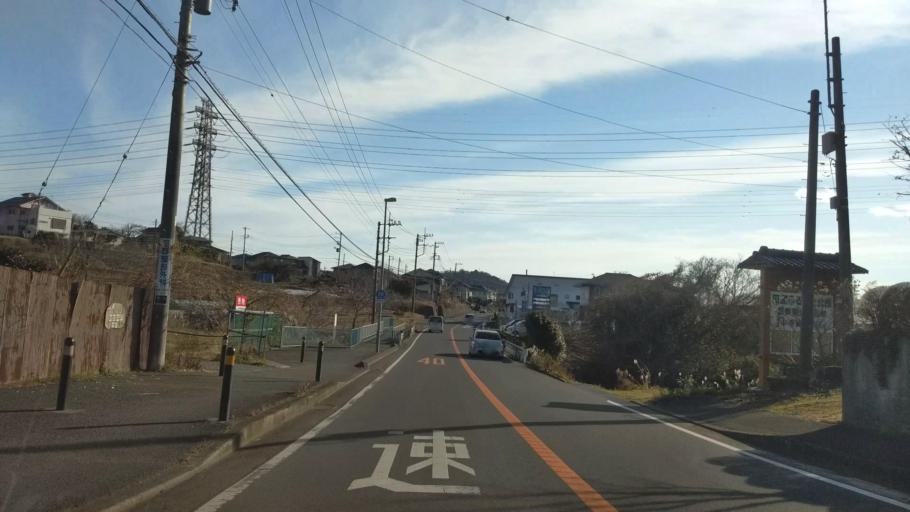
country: JP
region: Kanagawa
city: Hadano
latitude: 35.3901
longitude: 139.2350
